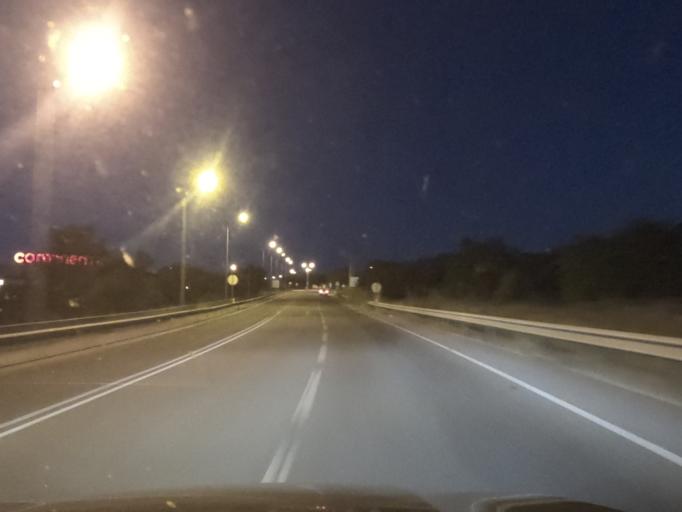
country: PT
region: Faro
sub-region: Loule
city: Loule
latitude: 37.1286
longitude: -8.0076
